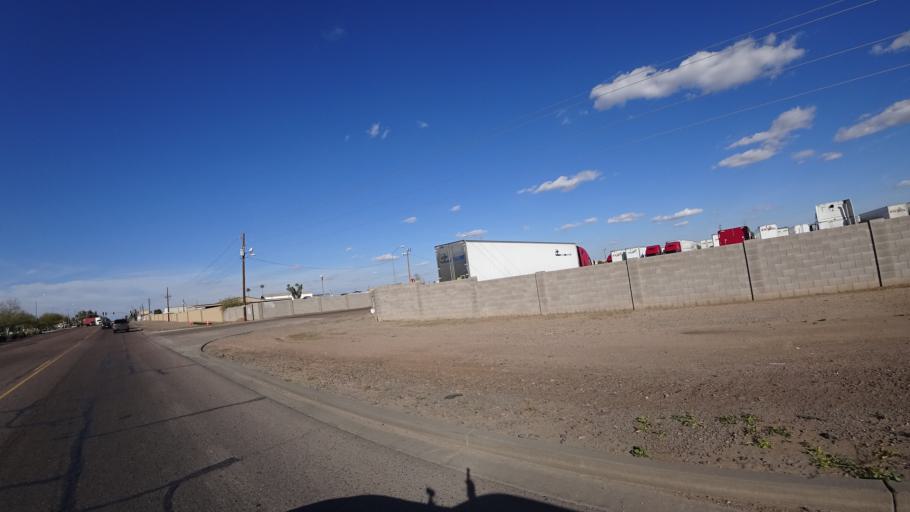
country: US
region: Arizona
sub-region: Maricopa County
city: Tolleson
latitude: 33.4384
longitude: -112.2382
